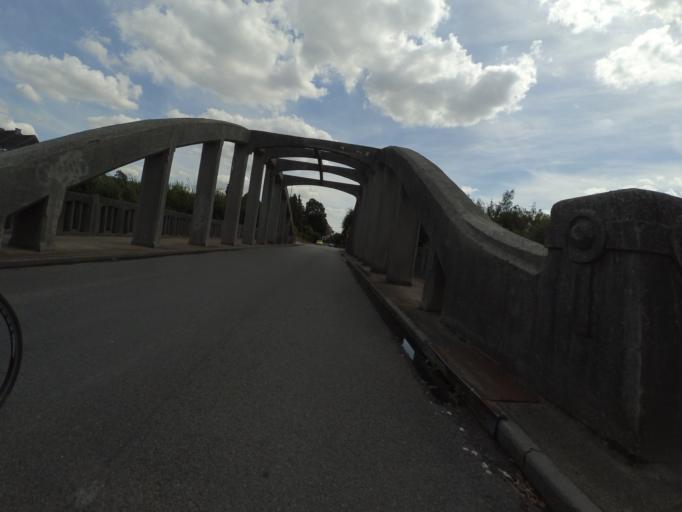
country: BE
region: Flanders
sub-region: Provincie Oost-Vlaanderen
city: Ronse
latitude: 50.7410
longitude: 3.5975
